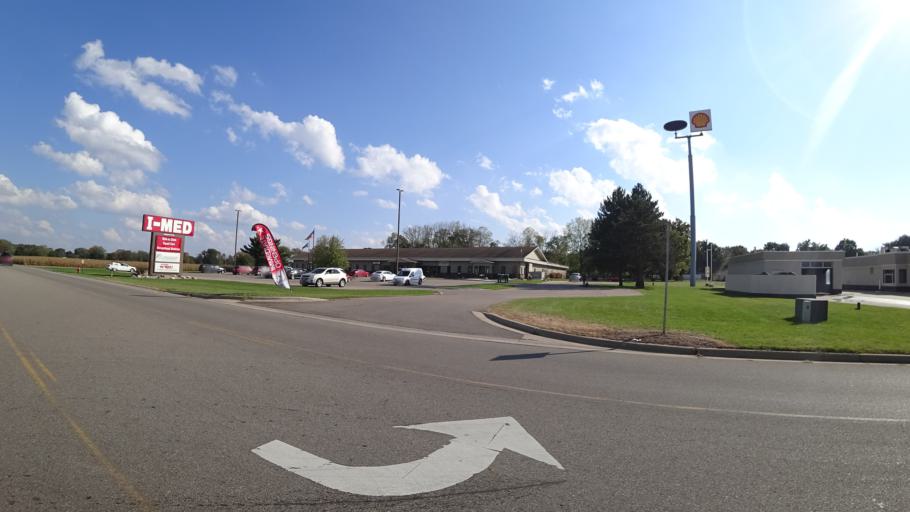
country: US
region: Michigan
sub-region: Saint Joseph County
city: Three Rivers
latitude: 41.9677
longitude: -85.6338
